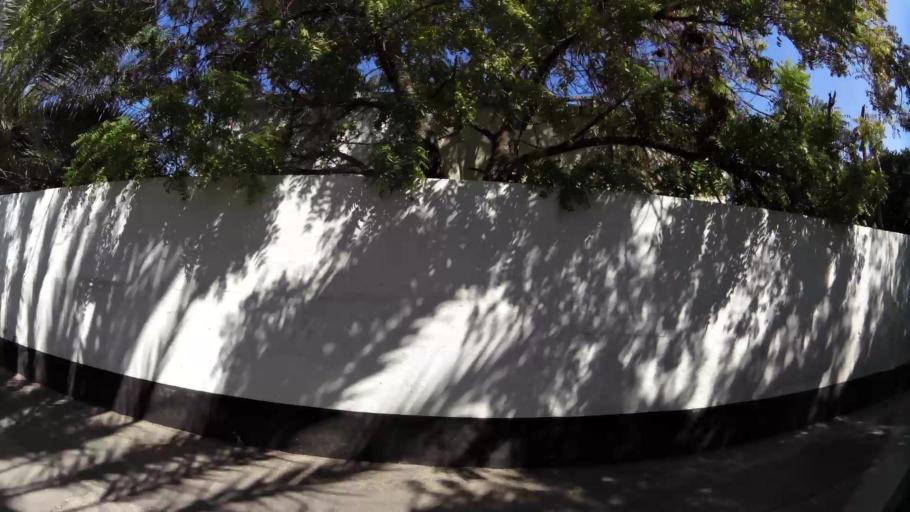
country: BH
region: Manama
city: Manama
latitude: 26.2144
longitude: 50.5830
